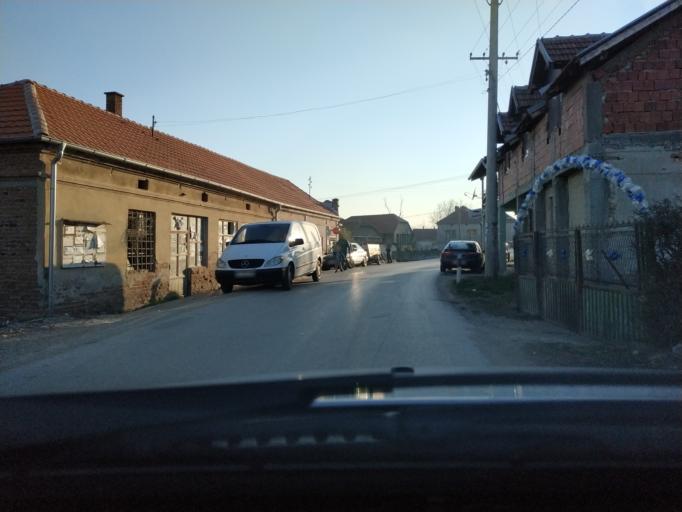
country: RS
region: Central Serbia
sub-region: Nisavski Okrug
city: Aleksinac
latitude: 43.4940
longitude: 21.7842
